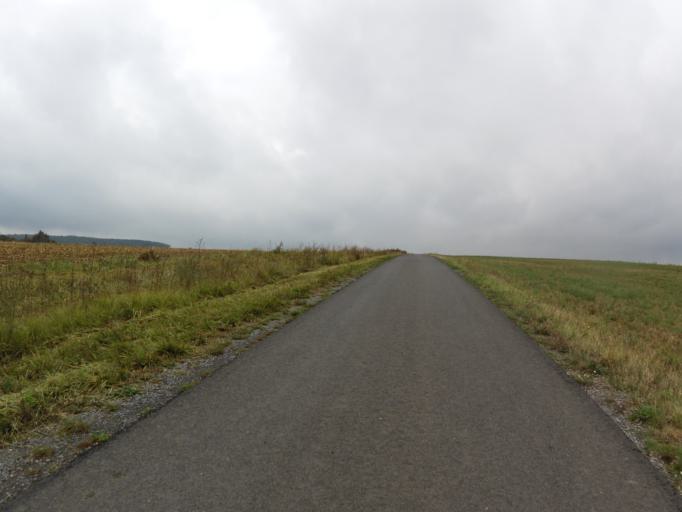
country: DE
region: Bavaria
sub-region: Regierungsbezirk Unterfranken
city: Gadheim
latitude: 49.8488
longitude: 9.9183
